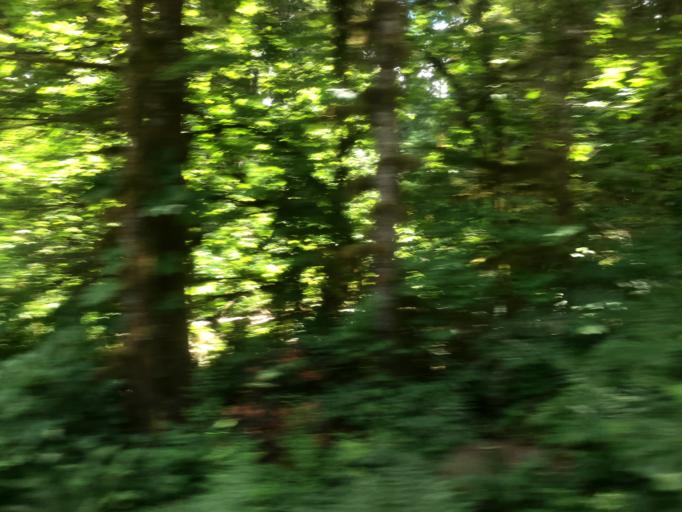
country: US
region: Oregon
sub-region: Clackamas County
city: Mount Hood Village
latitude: 45.4900
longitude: -122.0400
